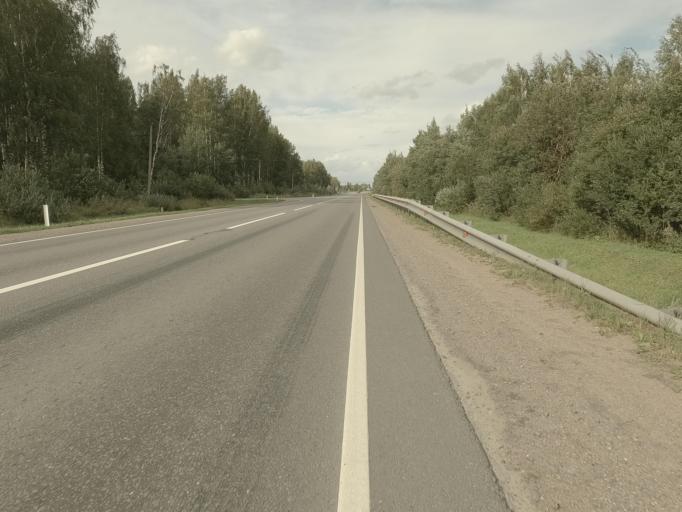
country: RU
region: Leningrad
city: Mga
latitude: 59.7889
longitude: 31.1076
